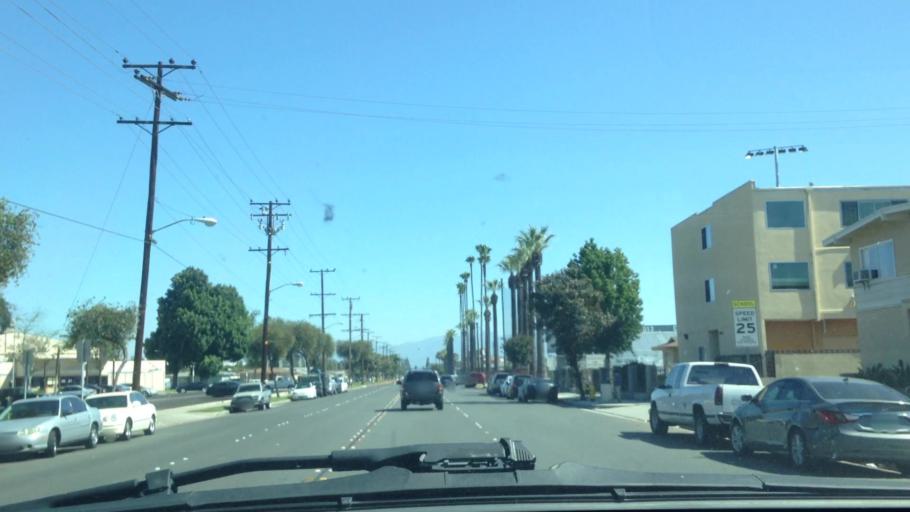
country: US
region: California
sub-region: Los Angeles County
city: Bellflower
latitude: 33.9043
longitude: -118.1253
